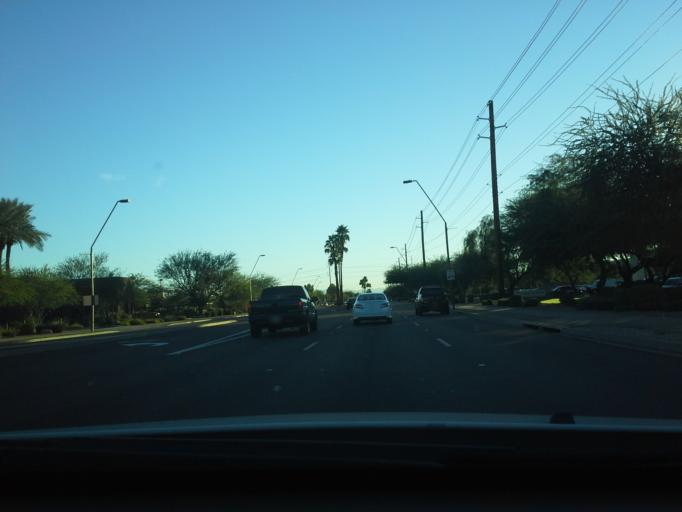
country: US
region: Arizona
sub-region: Maricopa County
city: Guadalupe
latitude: 33.3491
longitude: -111.9531
